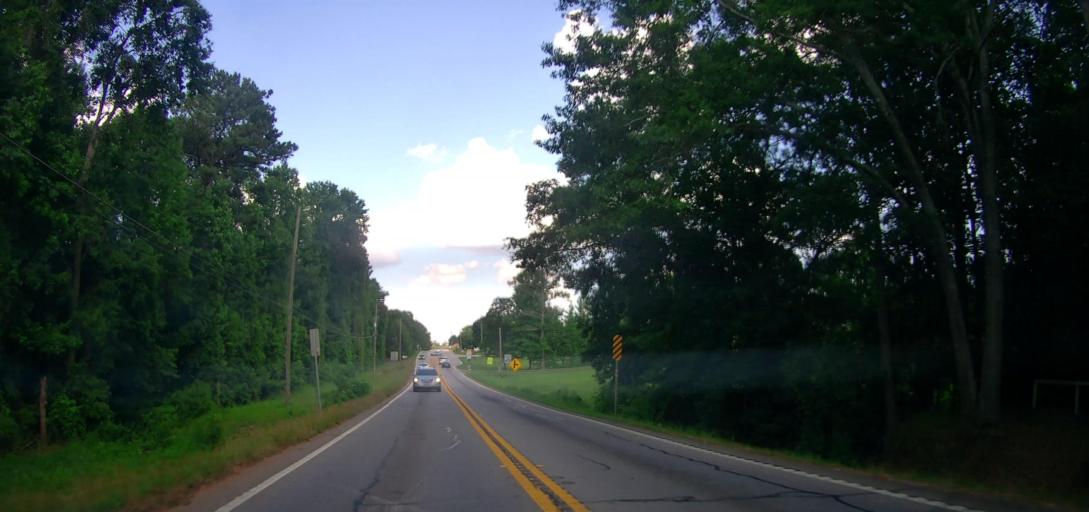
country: US
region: Georgia
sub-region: Henry County
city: McDonough
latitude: 33.4318
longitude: -84.2006
